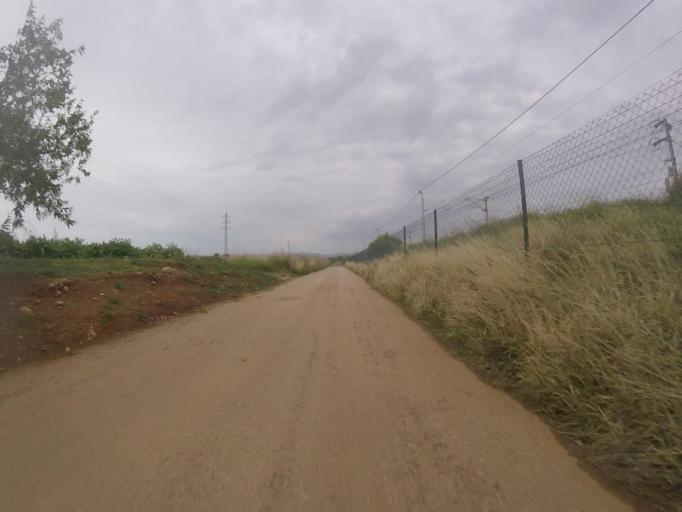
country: ES
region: Valencia
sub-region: Provincia de Castello
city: Torreblanca
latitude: 40.2161
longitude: 0.2037
